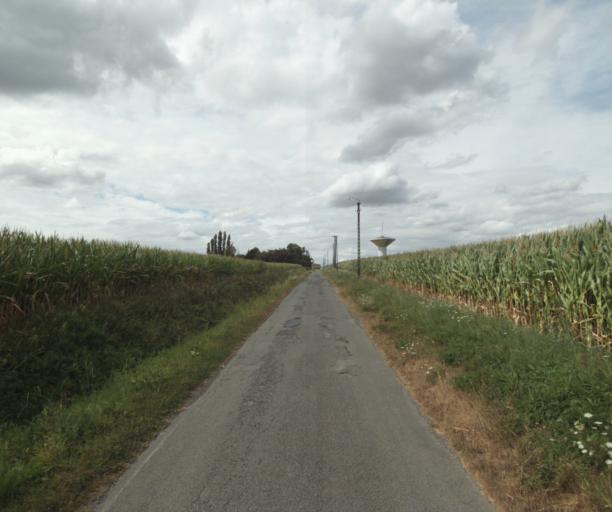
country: FR
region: Nord-Pas-de-Calais
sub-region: Departement du Nord
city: Bousbecque
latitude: 50.7648
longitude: 3.1040
